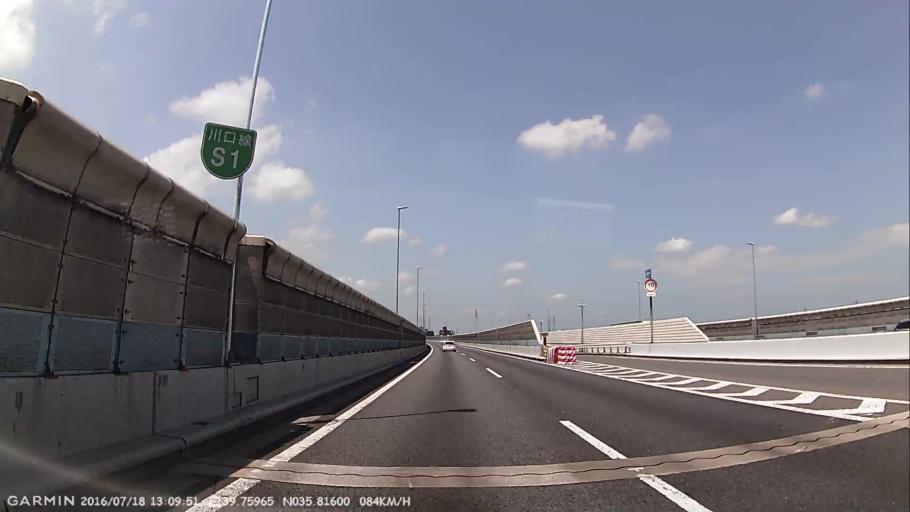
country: JP
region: Saitama
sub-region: Kawaguchi-shi
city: Hatogaya-honcho
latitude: 35.8162
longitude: 139.7597
